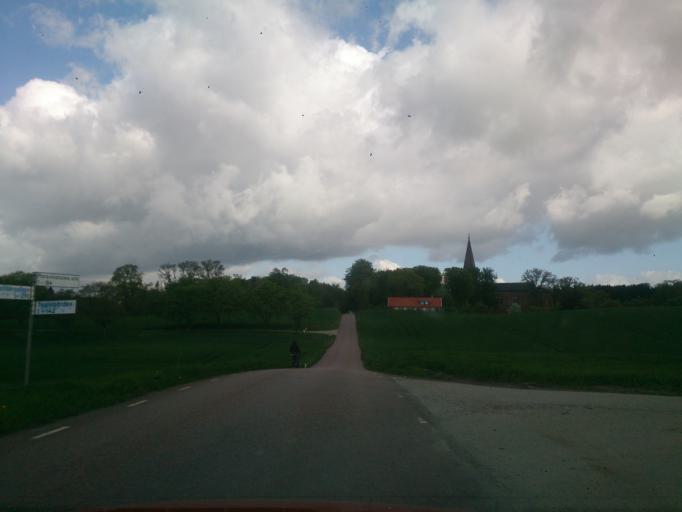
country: SE
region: Skane
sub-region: Ystads Kommun
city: Ystad
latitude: 55.4527
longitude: 13.7123
